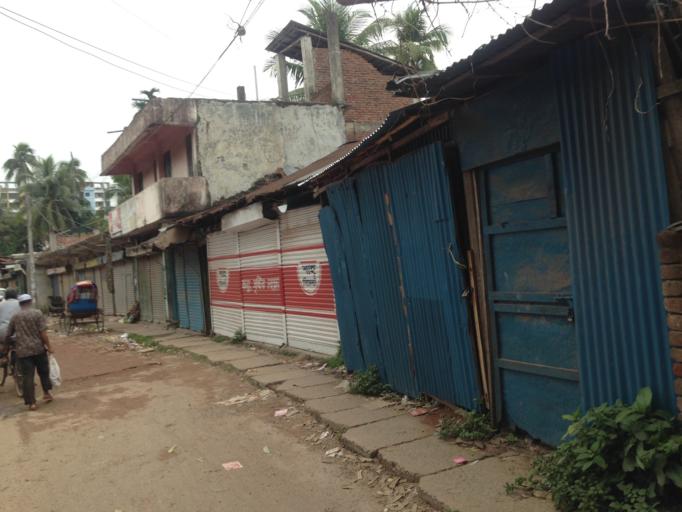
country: BD
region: Chittagong
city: Raipur
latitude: 23.0364
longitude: 90.7697
